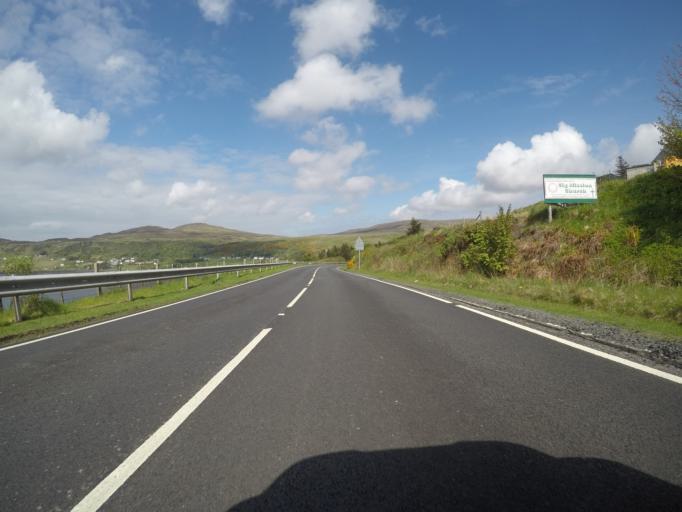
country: GB
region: Scotland
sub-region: Highland
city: Portree
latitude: 57.5813
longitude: -6.3601
